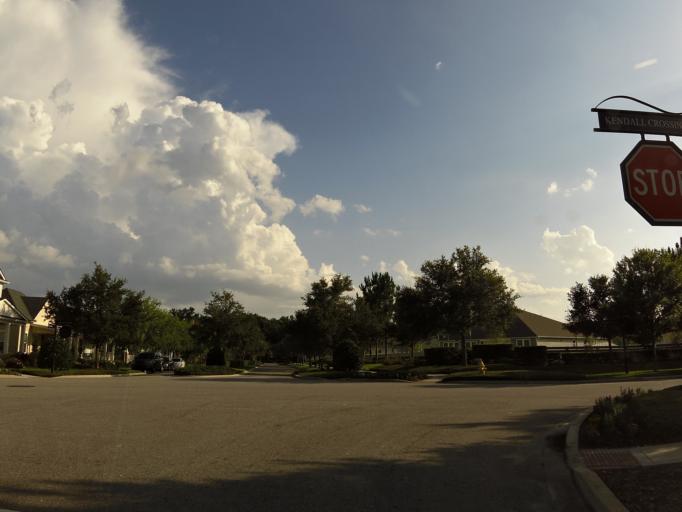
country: US
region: Florida
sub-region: Clay County
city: Green Cove Springs
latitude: 30.0217
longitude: -81.6365
